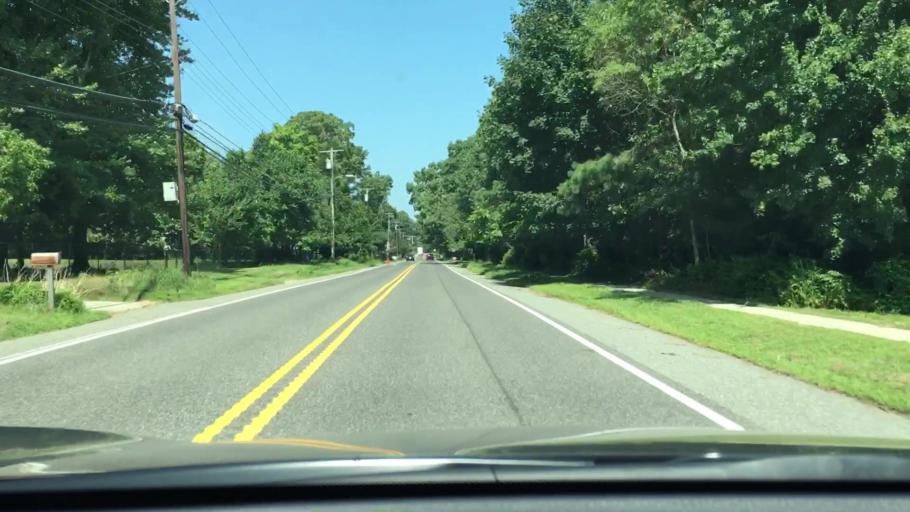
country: US
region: New Jersey
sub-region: Cumberland County
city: Millville
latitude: 39.3825
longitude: -75.0709
